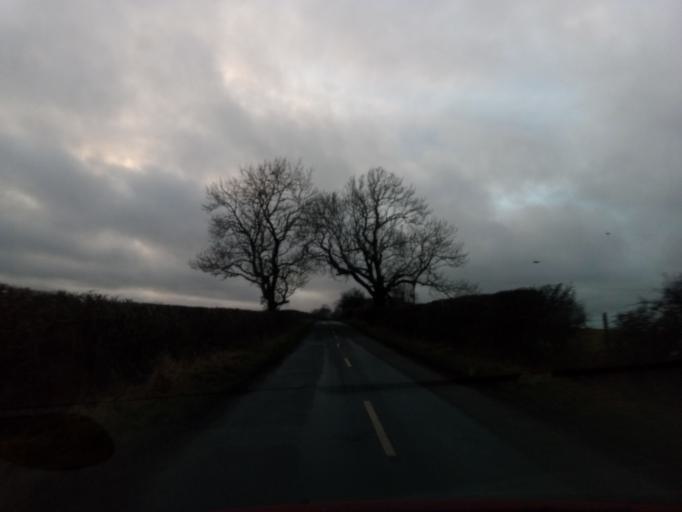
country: GB
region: England
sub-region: Northumberland
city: Meldon
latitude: 55.1413
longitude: -1.8254
